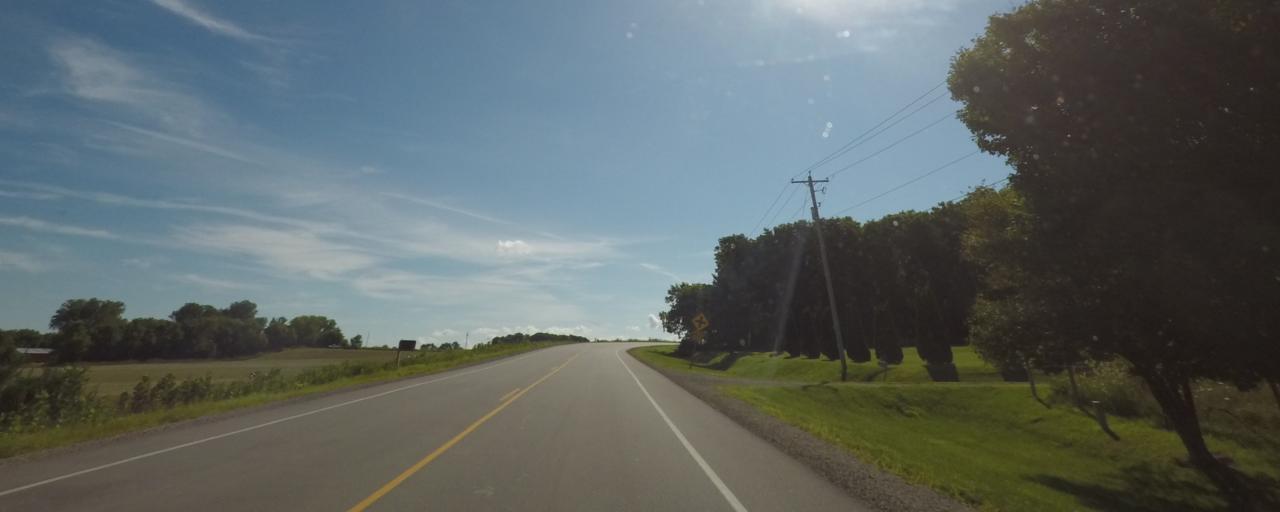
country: US
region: Wisconsin
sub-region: Jefferson County
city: Johnson Creek
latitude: 43.0772
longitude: -88.7510
